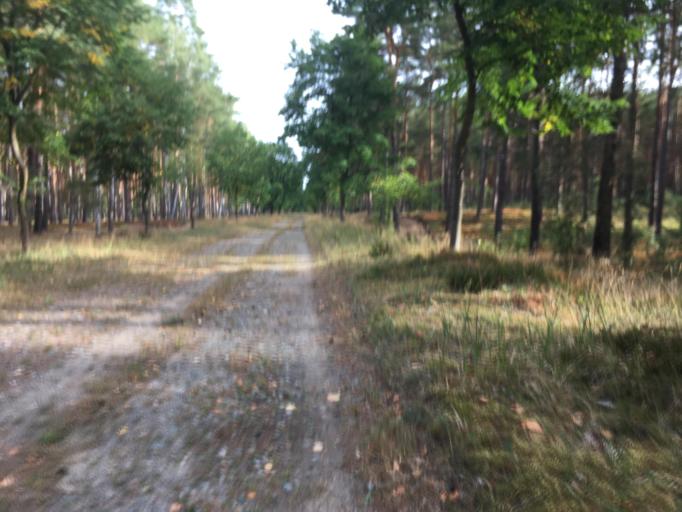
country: DE
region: Brandenburg
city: Marienwerder
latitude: 52.9529
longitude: 13.5246
